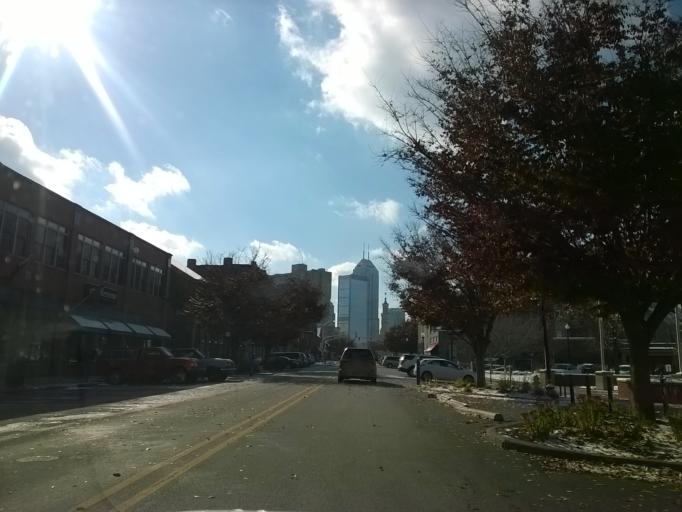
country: US
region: Indiana
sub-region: Marion County
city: Indianapolis
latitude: 39.7773
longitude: -86.1458
